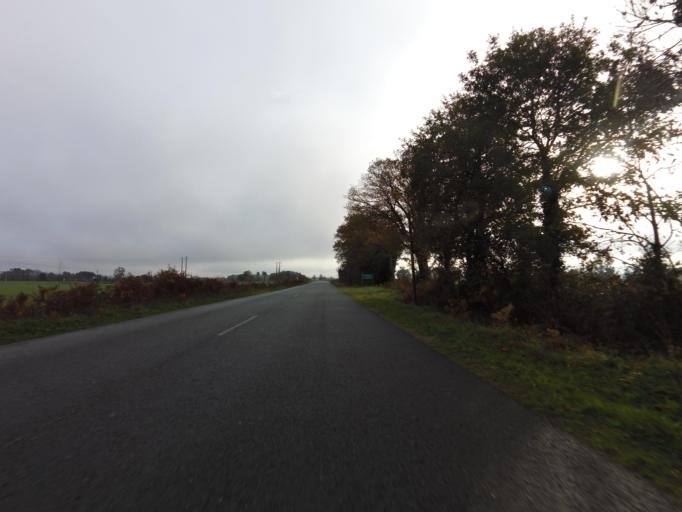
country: FR
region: Brittany
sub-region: Departement du Morbihan
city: Saint-Martin-sur-Oust
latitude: 47.7204
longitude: -2.2507
